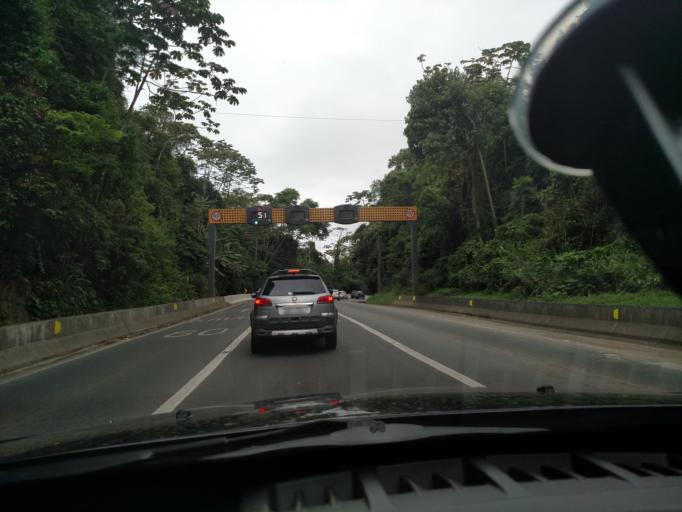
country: BR
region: Santa Catarina
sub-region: Itapema
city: Itapema
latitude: -27.0432
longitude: -48.5994
